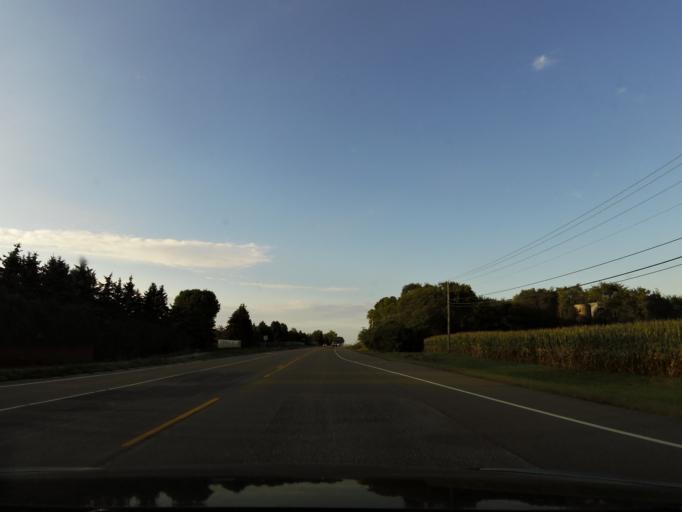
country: US
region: Minnesota
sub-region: Washington County
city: Cottage Grove
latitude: 44.8410
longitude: -92.9038
